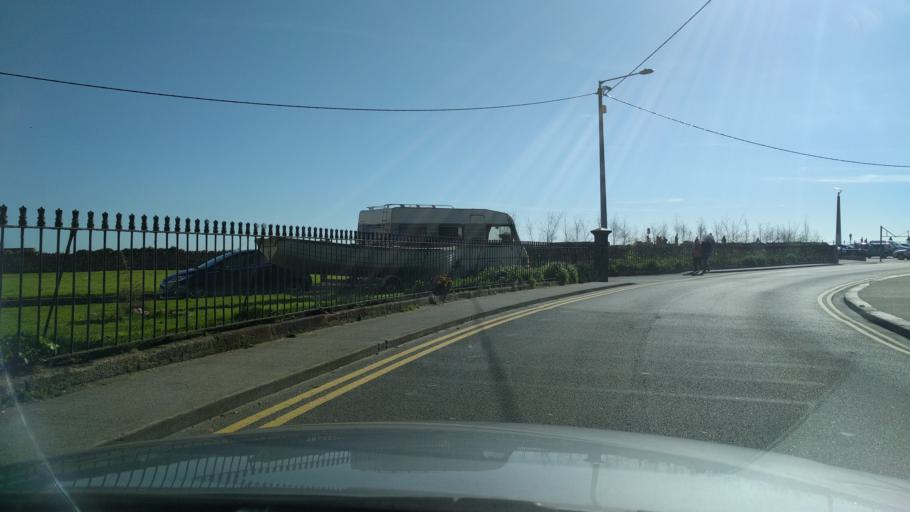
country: IE
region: Leinster
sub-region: Wicklow
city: Bray
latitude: 53.2073
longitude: -6.1013
